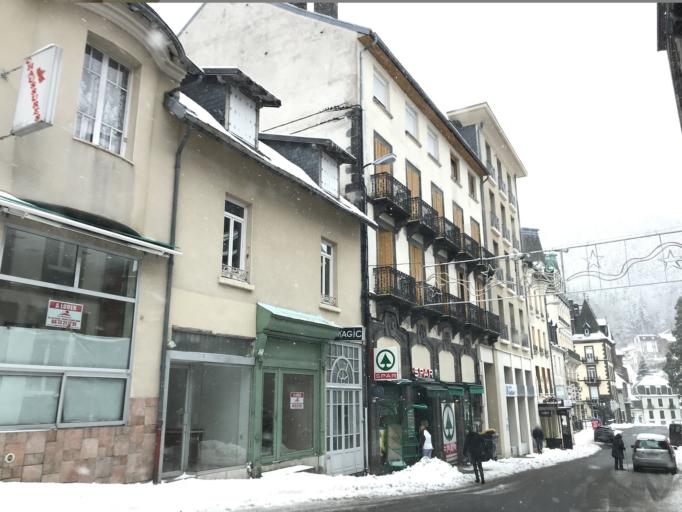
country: FR
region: Auvergne
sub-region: Departement du Puy-de-Dome
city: Mont-Dore
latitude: 45.5751
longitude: 2.8102
